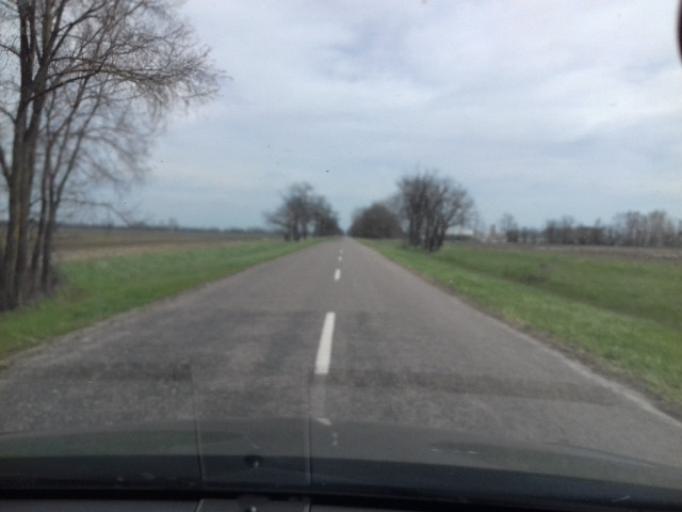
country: HU
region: Jasz-Nagykun-Szolnok
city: Cserkeszolo
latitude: 46.9019
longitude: 20.1682
